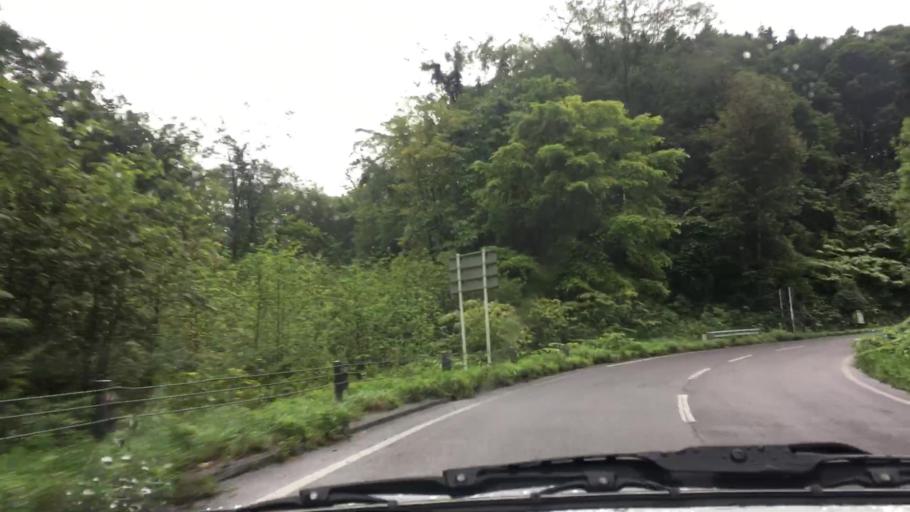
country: JP
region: Hokkaido
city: Niseko Town
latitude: 42.6275
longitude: 140.7232
